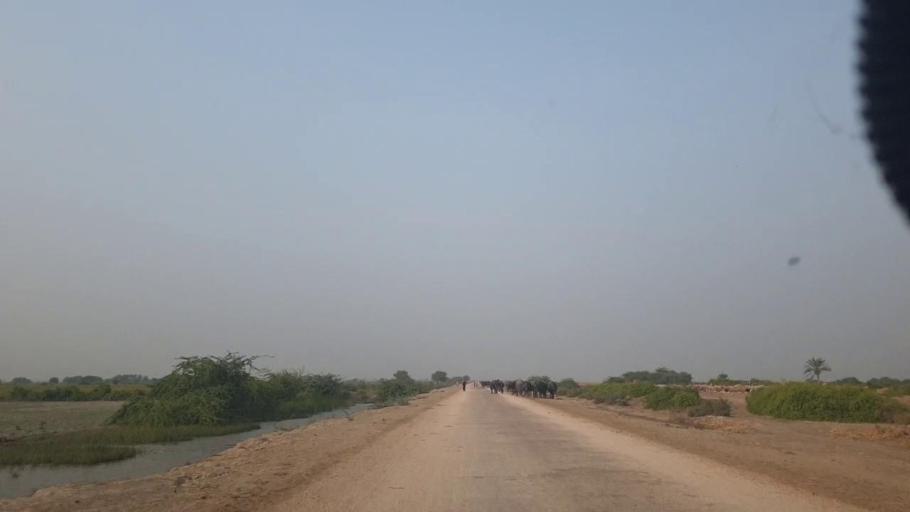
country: PK
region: Sindh
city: Bulri
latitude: 24.8398
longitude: 68.4036
